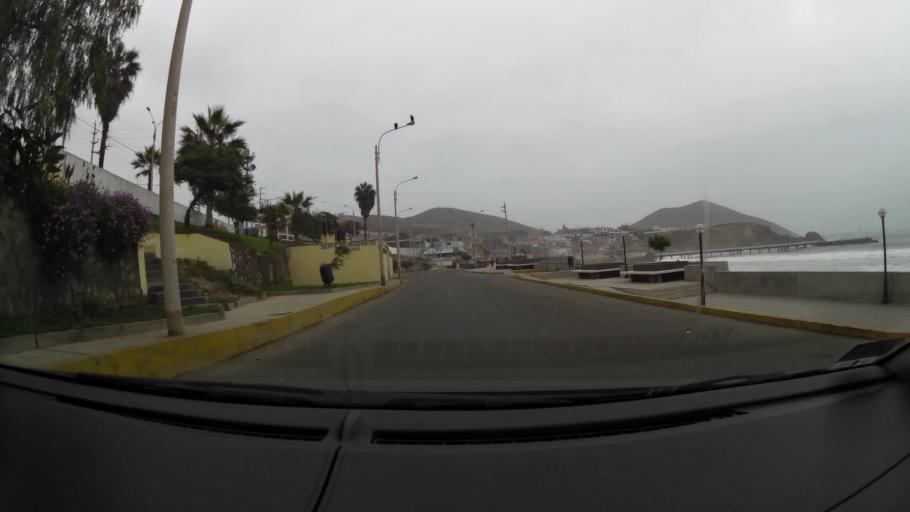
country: PE
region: Lima
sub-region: Provincia de Huaral
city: Chancay
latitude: -11.5845
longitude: -77.2710
